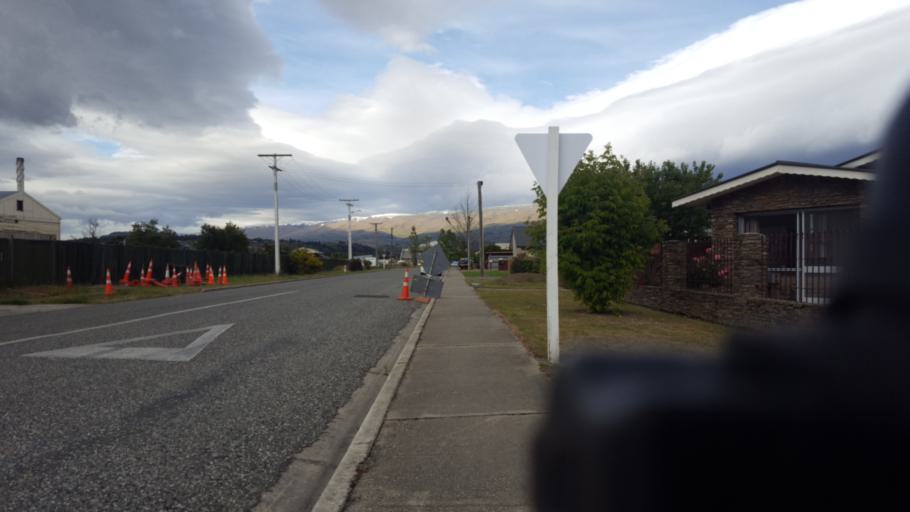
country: NZ
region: Otago
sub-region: Queenstown-Lakes District
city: Wanaka
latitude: -45.2433
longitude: 169.3949
